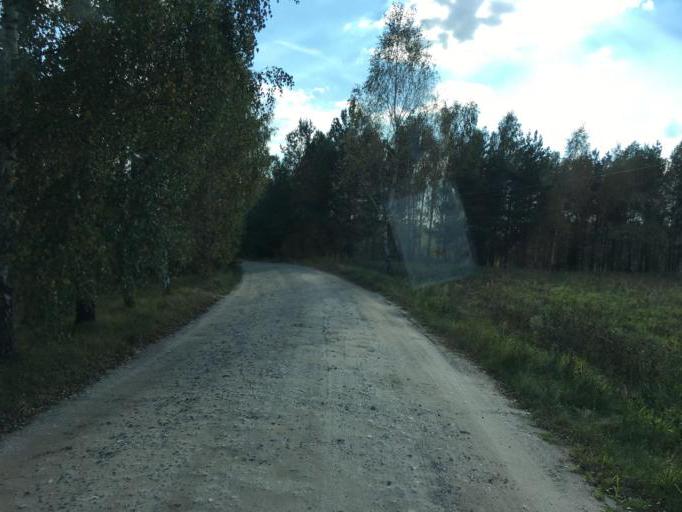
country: PL
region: Kujawsko-Pomorskie
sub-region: Powiat tucholski
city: Tuchola
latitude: 53.6064
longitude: 17.9124
